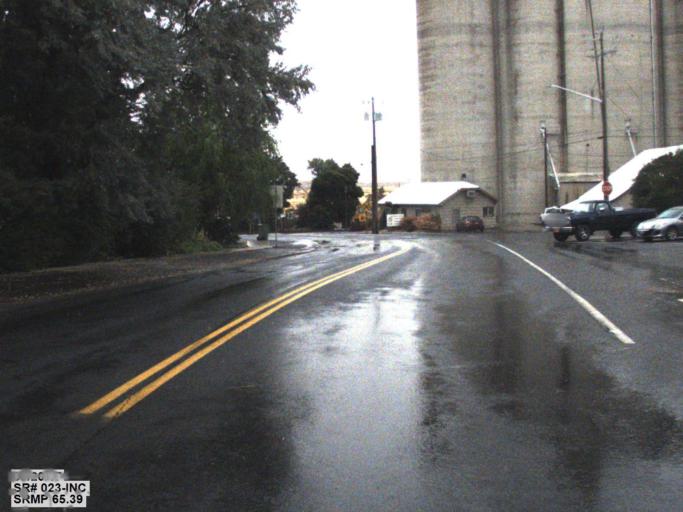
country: US
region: Washington
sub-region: Lincoln County
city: Davenport
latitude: 47.4785
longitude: -118.2518
